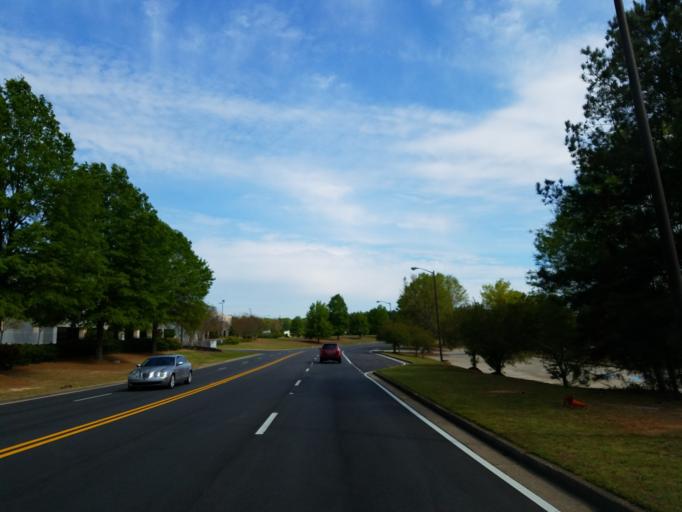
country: US
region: Georgia
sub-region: Cobb County
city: Austell
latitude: 33.7851
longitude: -84.6227
